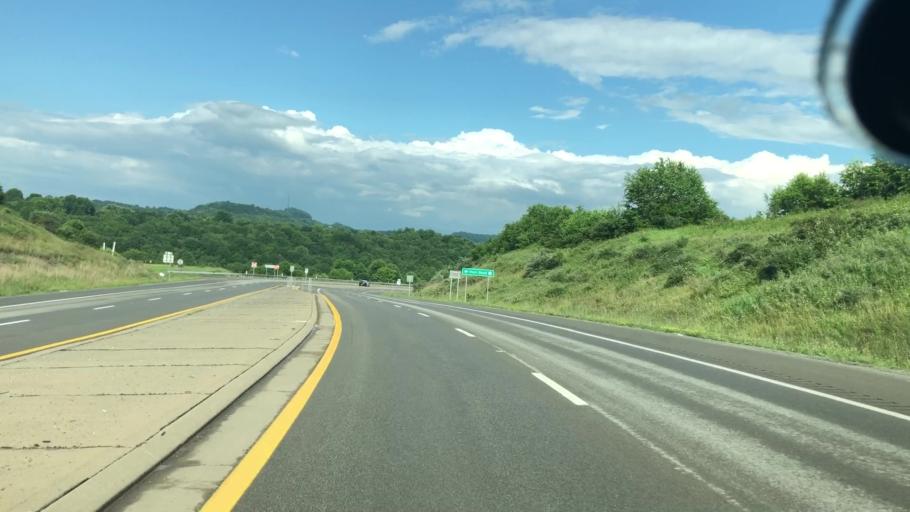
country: US
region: West Virginia
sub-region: Harrison County
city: Bridgeport
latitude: 39.3034
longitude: -80.2119
